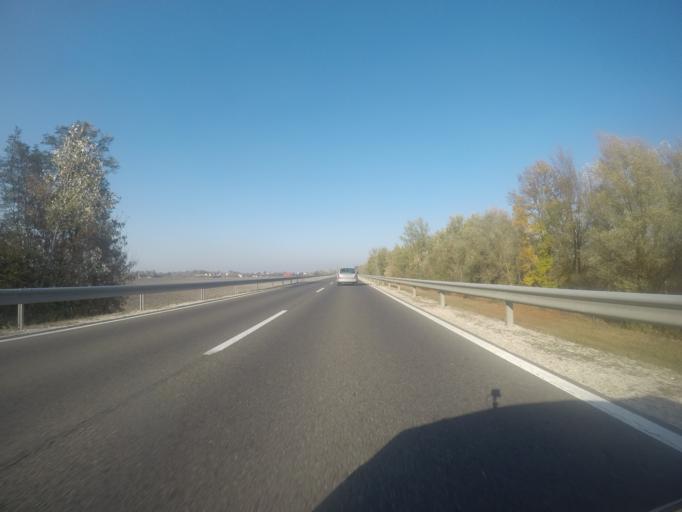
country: HU
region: Fejer
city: Ivancsa
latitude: 47.1726
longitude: 18.8662
